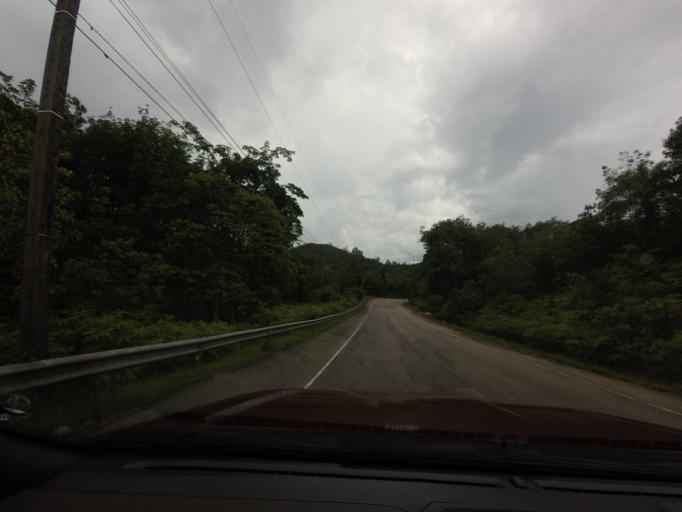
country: TH
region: Narathiwat
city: Sukhirin
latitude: 5.9798
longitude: 101.6975
